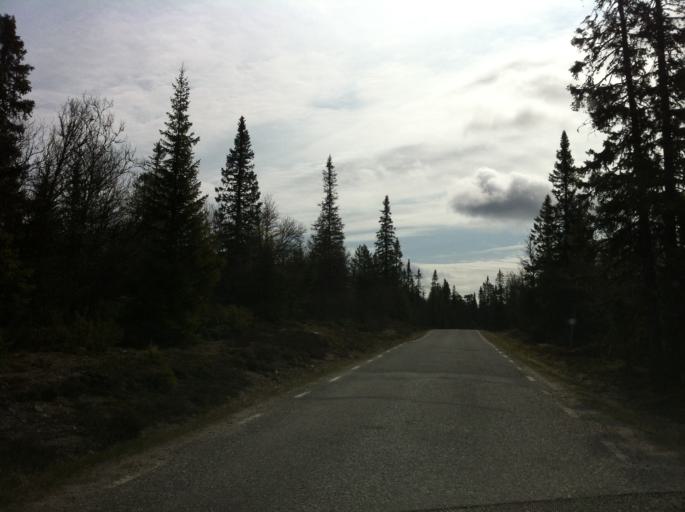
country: NO
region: Hedmark
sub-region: Engerdal
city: Engerdal
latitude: 62.3086
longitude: 12.8070
